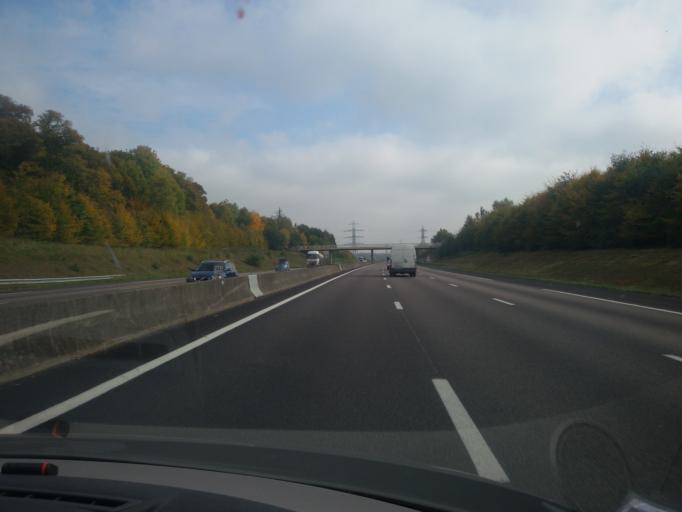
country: FR
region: Haute-Normandie
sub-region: Departement de l'Eure
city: Saint-Ouen-de-Thouberville
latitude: 49.3482
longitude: 0.9052
